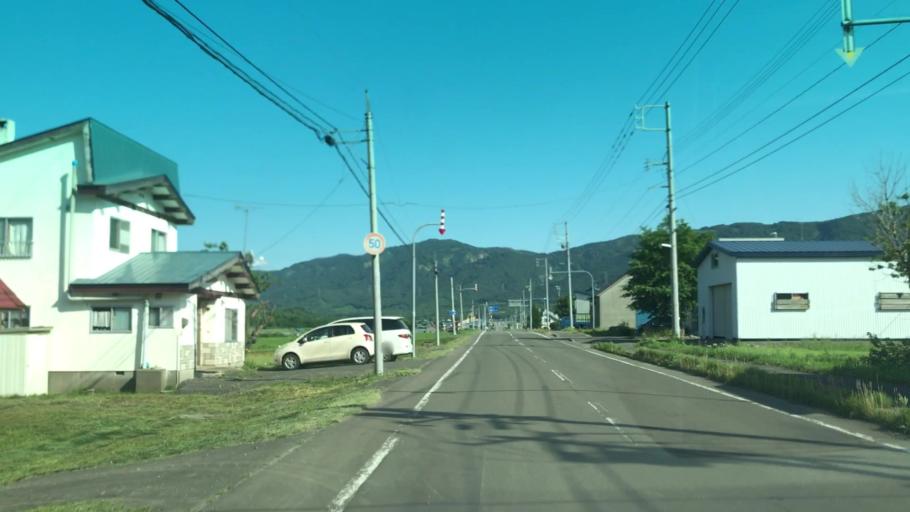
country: JP
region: Hokkaido
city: Yoichi
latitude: 43.0563
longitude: 140.7166
